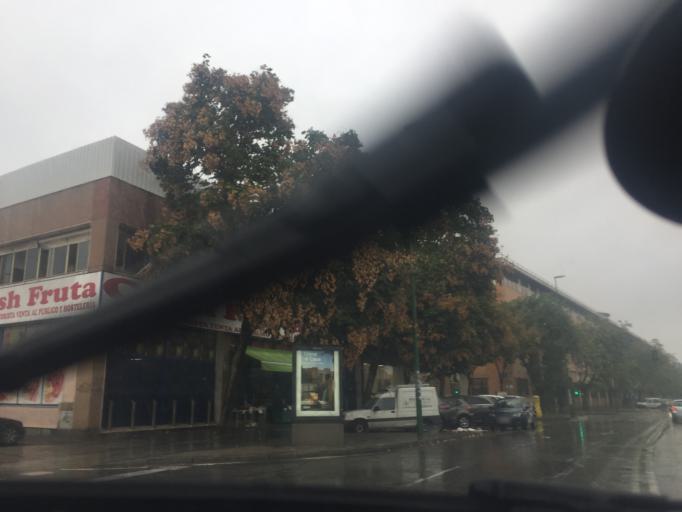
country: ES
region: Andalusia
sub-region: Provincia de Sevilla
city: Sevilla
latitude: 37.3689
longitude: -5.9573
